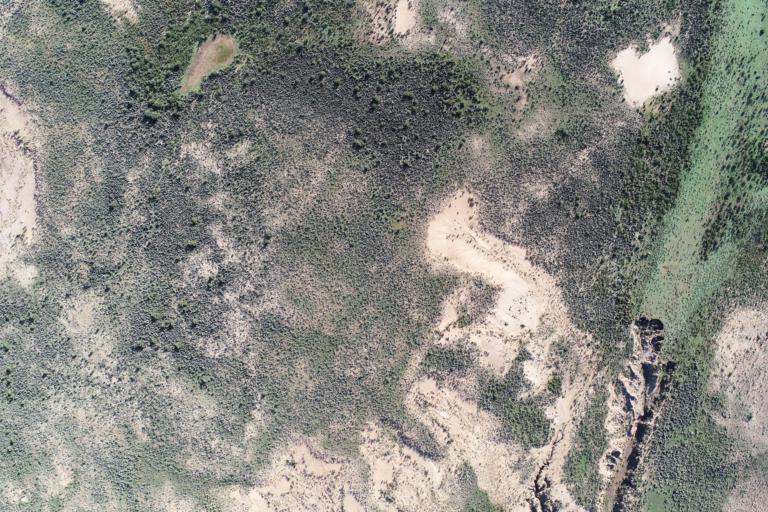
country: BO
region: La Paz
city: Curahuara de Carangas
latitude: -17.3013
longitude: -68.5118
